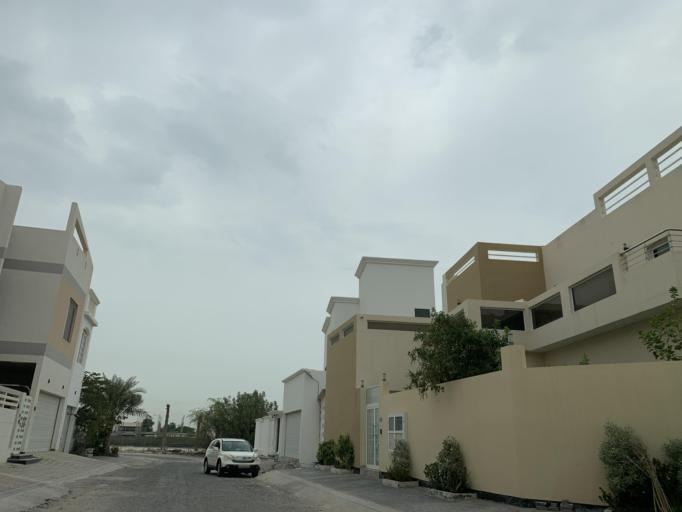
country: BH
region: Northern
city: Madinat `Isa
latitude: 26.1951
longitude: 50.4775
